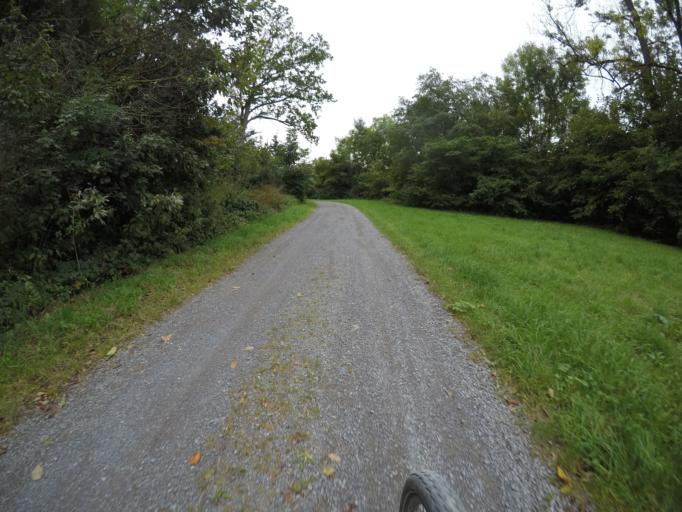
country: DE
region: Baden-Wuerttemberg
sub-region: Regierungsbezirk Stuttgart
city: Eberdingen
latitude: 48.9034
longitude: 8.9791
